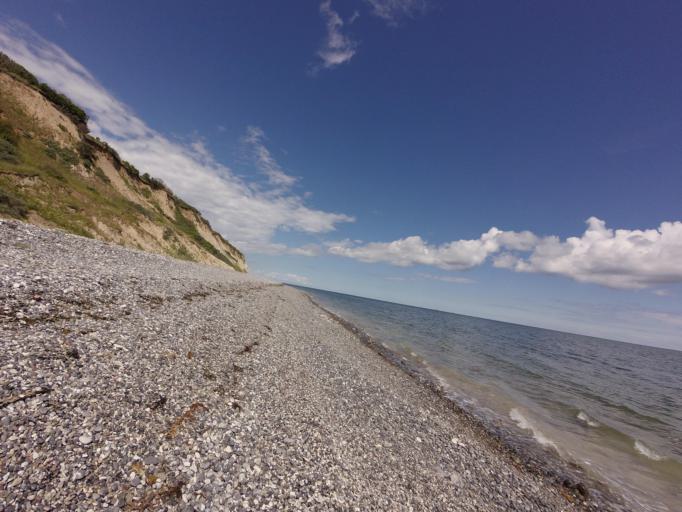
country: DK
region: Central Jutland
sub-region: Norddjurs Kommune
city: Grenaa
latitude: 56.5145
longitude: 10.8645
